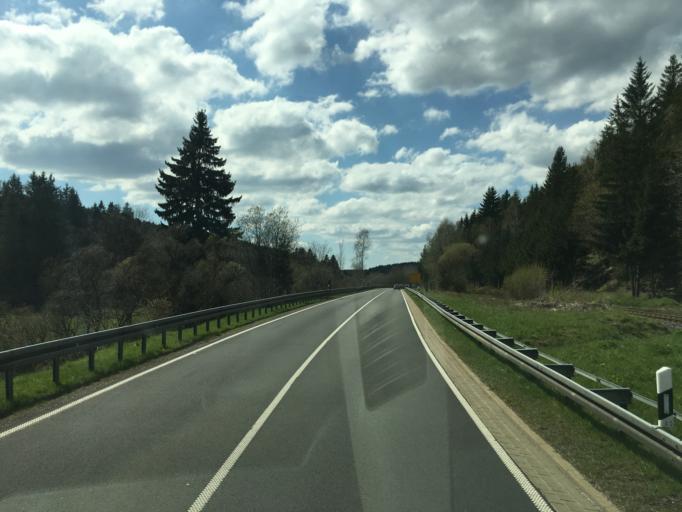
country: DE
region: Saxony-Anhalt
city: Benneckenstein
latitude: 51.6969
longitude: 10.6919
